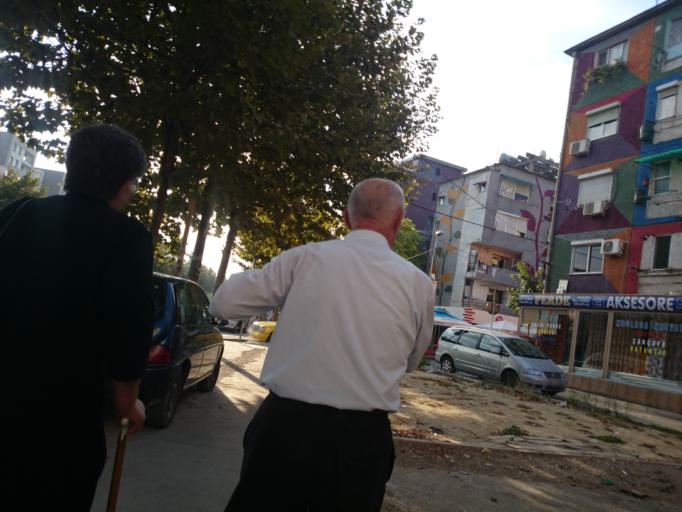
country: AL
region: Tirane
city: Tirana
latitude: 41.3209
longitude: 19.7935
